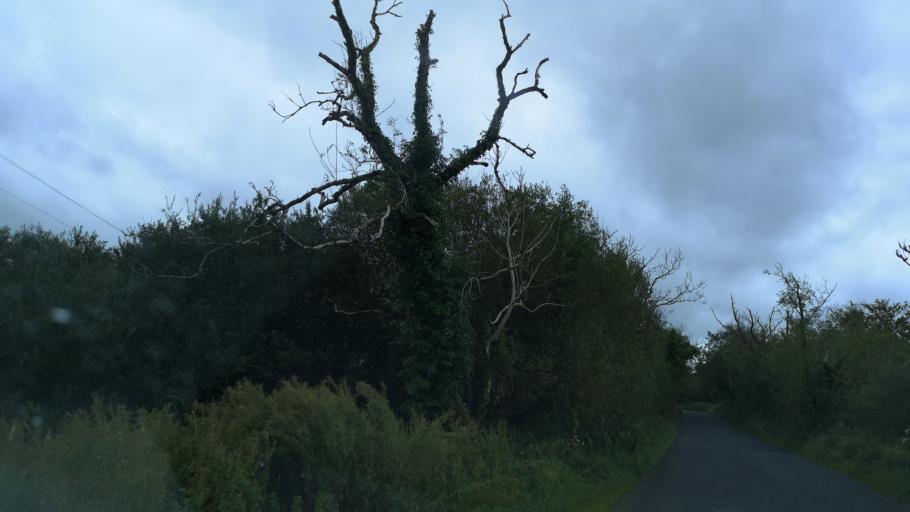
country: IE
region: Connaught
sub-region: County Galway
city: Loughrea
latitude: 53.2915
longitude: -8.5910
